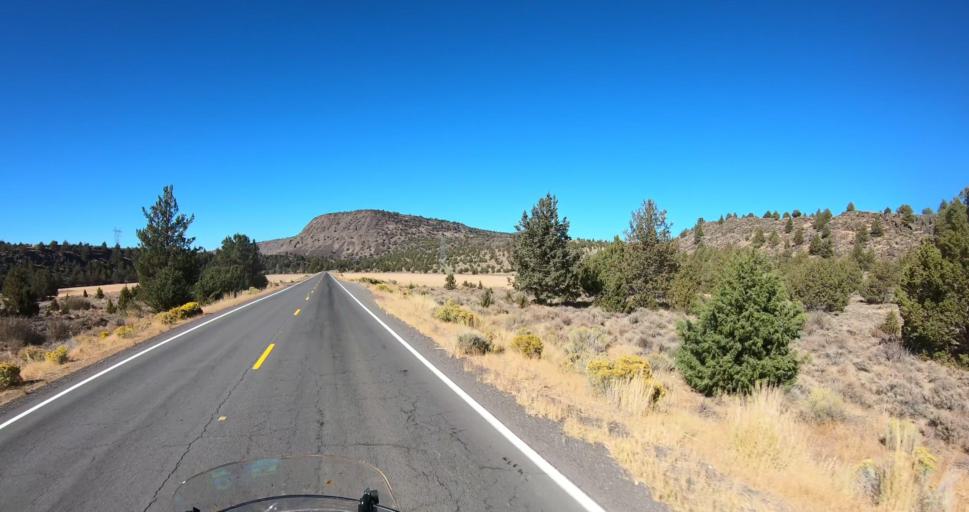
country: US
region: Oregon
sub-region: Deschutes County
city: La Pine
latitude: 43.0347
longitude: -120.7936
